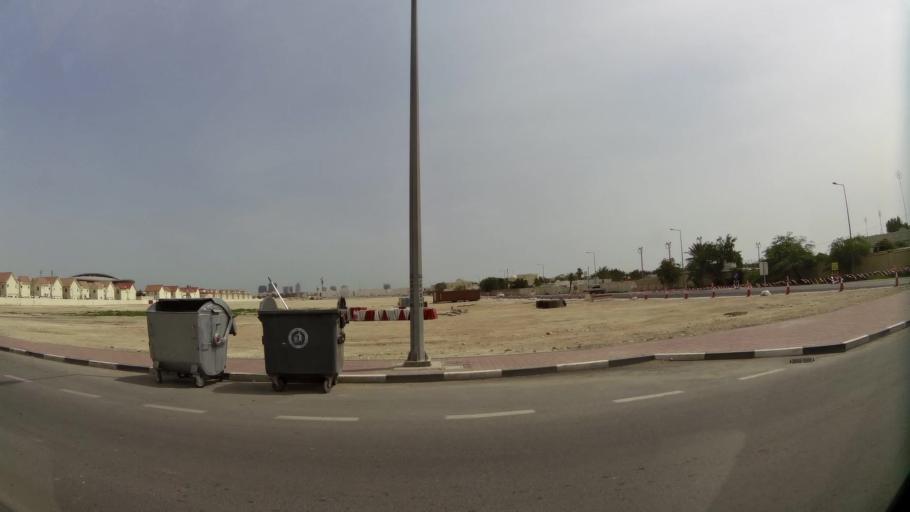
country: QA
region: Baladiyat ad Dawhah
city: Doha
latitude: 25.2648
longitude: 51.4872
